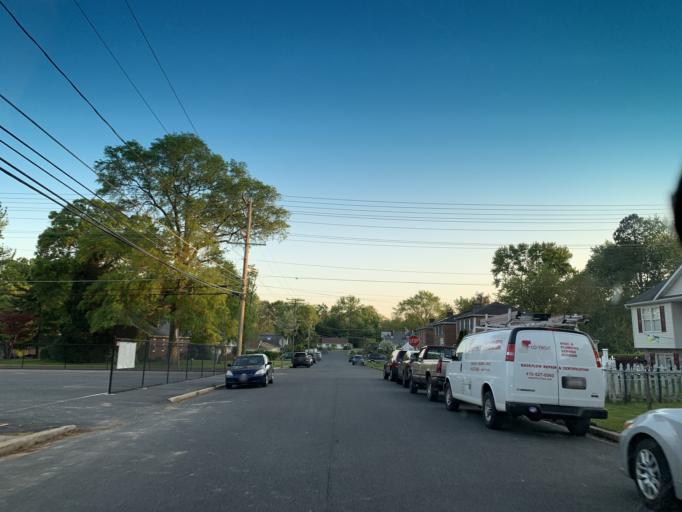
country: US
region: Maryland
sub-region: Harford County
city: Aberdeen
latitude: 39.5079
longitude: -76.1721
